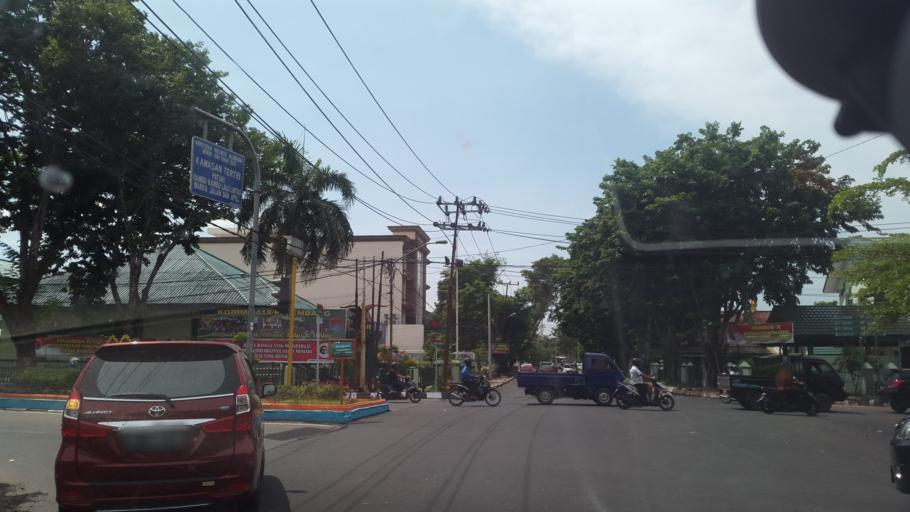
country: ID
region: South Sumatra
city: Plaju
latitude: -2.9902
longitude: 104.7498
